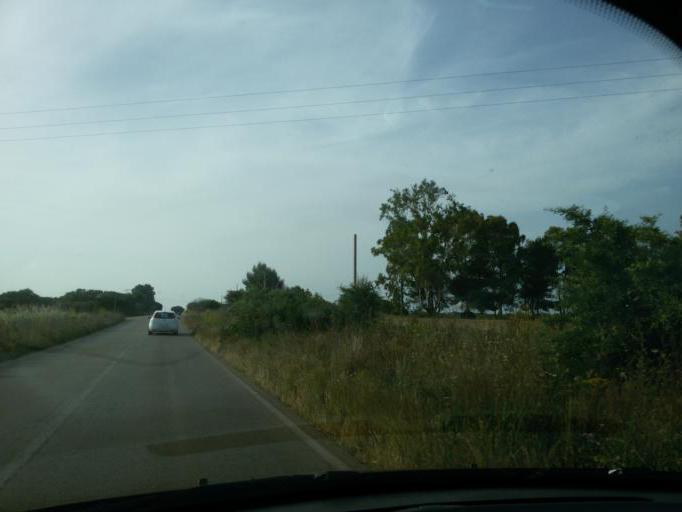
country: IT
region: Apulia
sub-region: Provincia di Brindisi
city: San Pancrazio Salentino
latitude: 40.3370
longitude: 17.8500
